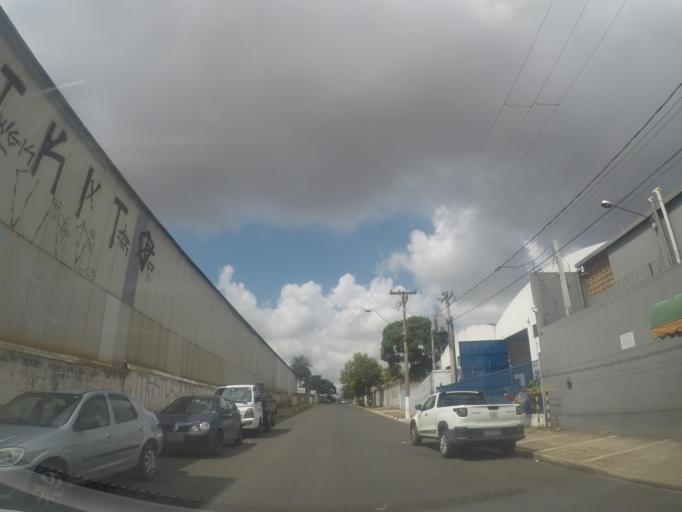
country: BR
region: Sao Paulo
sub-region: Hortolandia
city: Hortolandia
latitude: -22.8490
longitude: -47.1623
